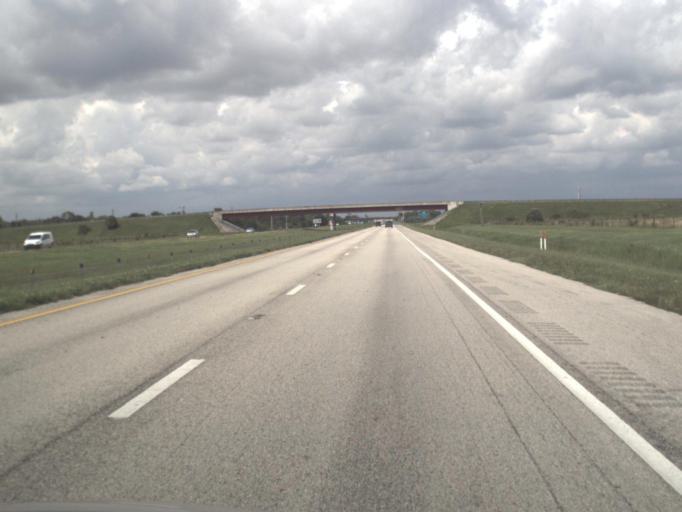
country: US
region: Florida
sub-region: Charlotte County
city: Punta Gorda
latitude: 26.9146
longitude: -82.0114
